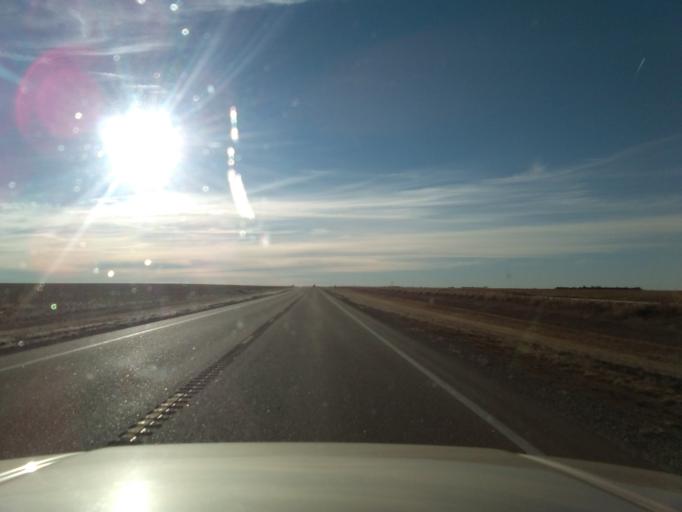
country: US
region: Kansas
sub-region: Sheridan County
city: Hoxie
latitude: 39.5183
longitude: -100.6277
